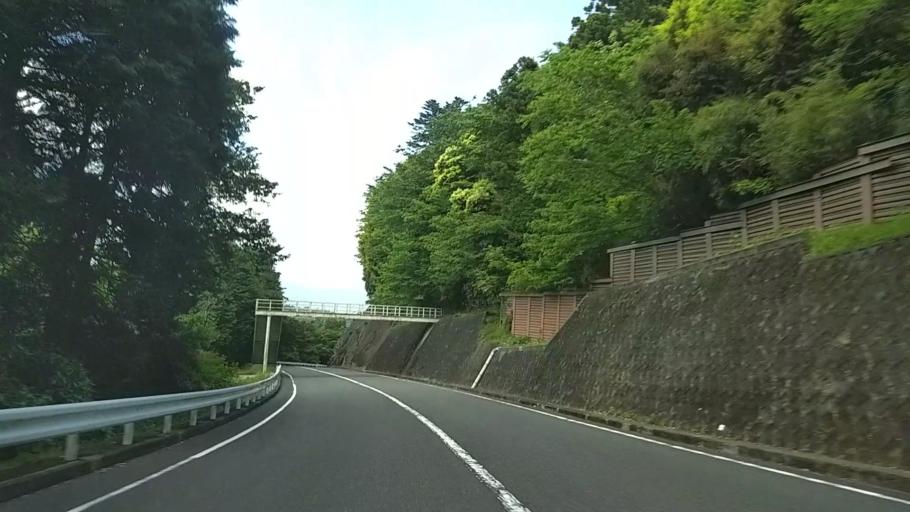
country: JP
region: Kanagawa
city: Odawara
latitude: 35.2336
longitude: 139.1260
